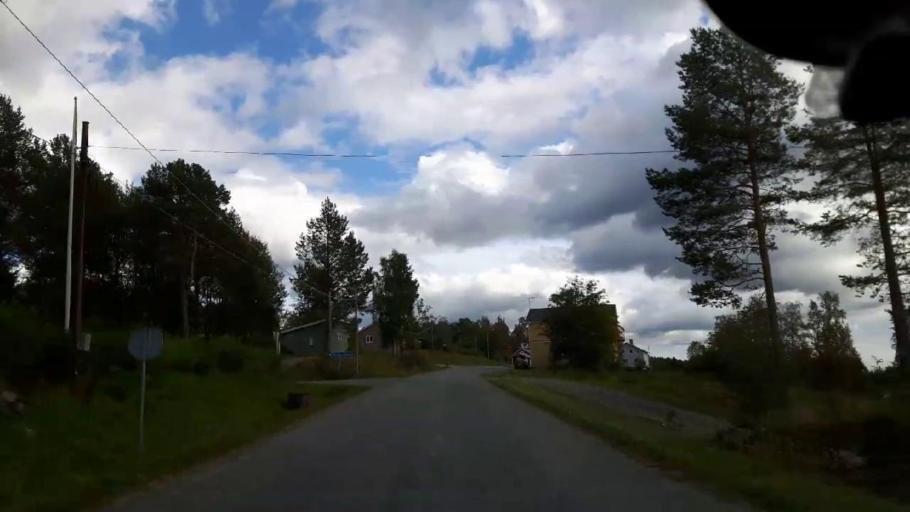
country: SE
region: Jaemtland
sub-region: Stroemsunds Kommun
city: Stroemsund
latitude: 63.4248
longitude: 15.8207
